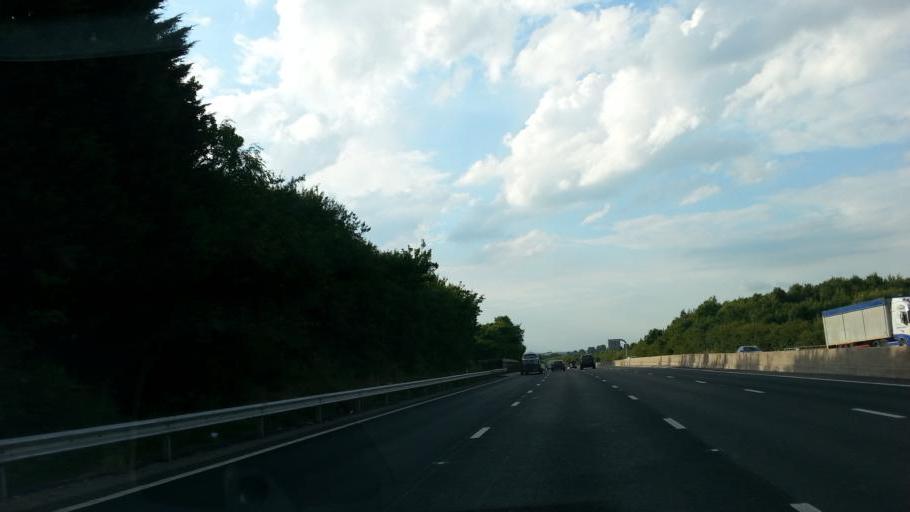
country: GB
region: England
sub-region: Worcestershire
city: Droitwich
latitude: 52.2526
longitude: -2.1342
